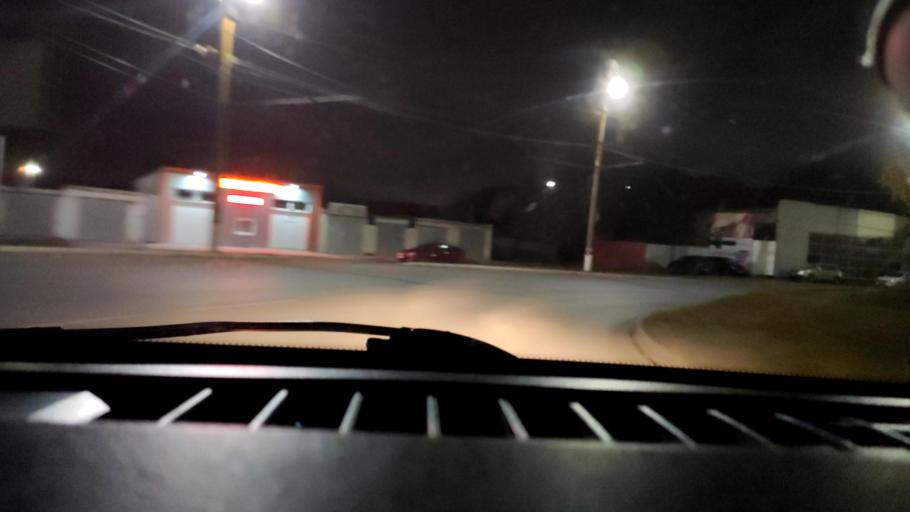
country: RU
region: Samara
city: Novokuybyshevsk
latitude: 53.1086
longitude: 49.9579
